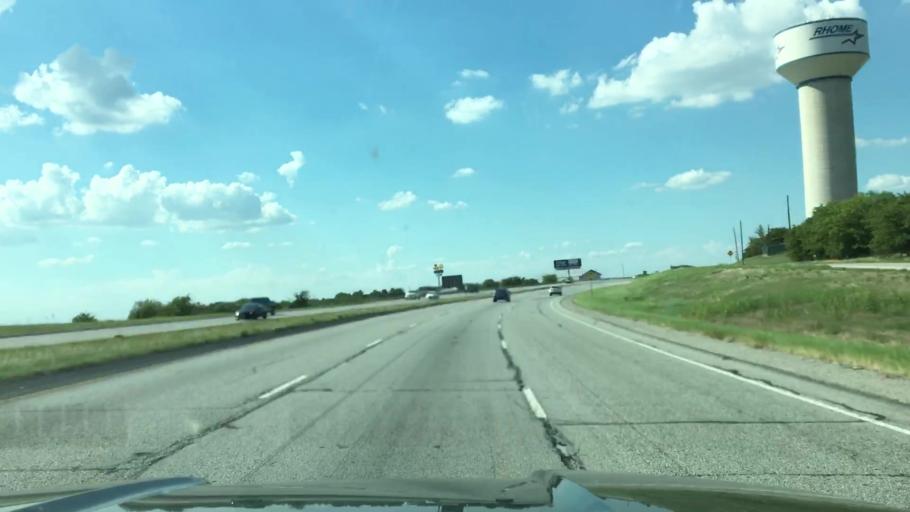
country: US
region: Texas
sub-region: Wise County
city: Rhome
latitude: 33.0490
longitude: -97.4766
